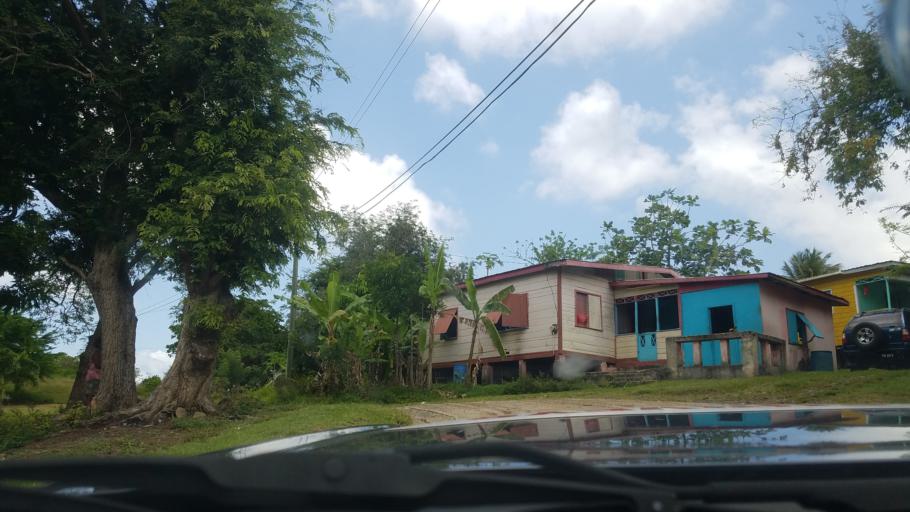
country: LC
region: Gros-Islet
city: Gros Islet
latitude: 14.0558
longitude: -60.9271
